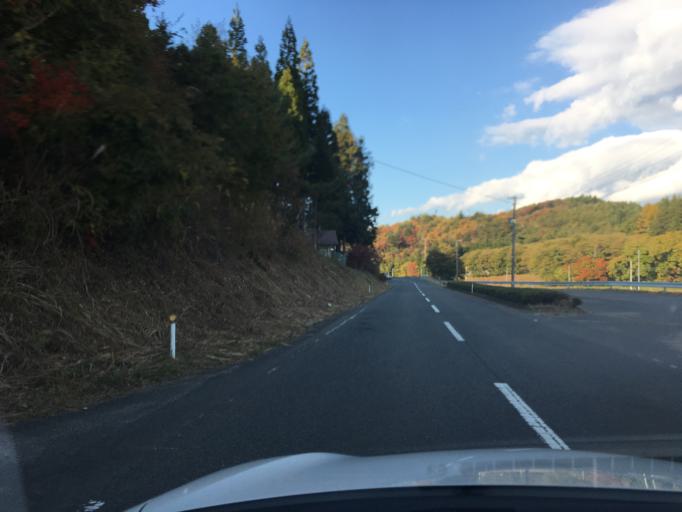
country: JP
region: Fukushima
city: Iwaki
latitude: 37.2664
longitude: 140.7647
